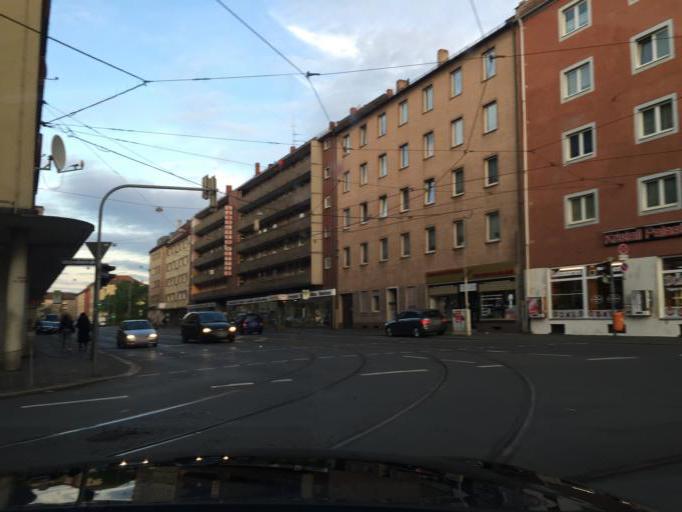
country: DE
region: Bavaria
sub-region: Regierungsbezirk Mittelfranken
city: Nuernberg
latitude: 49.4396
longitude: 11.0672
